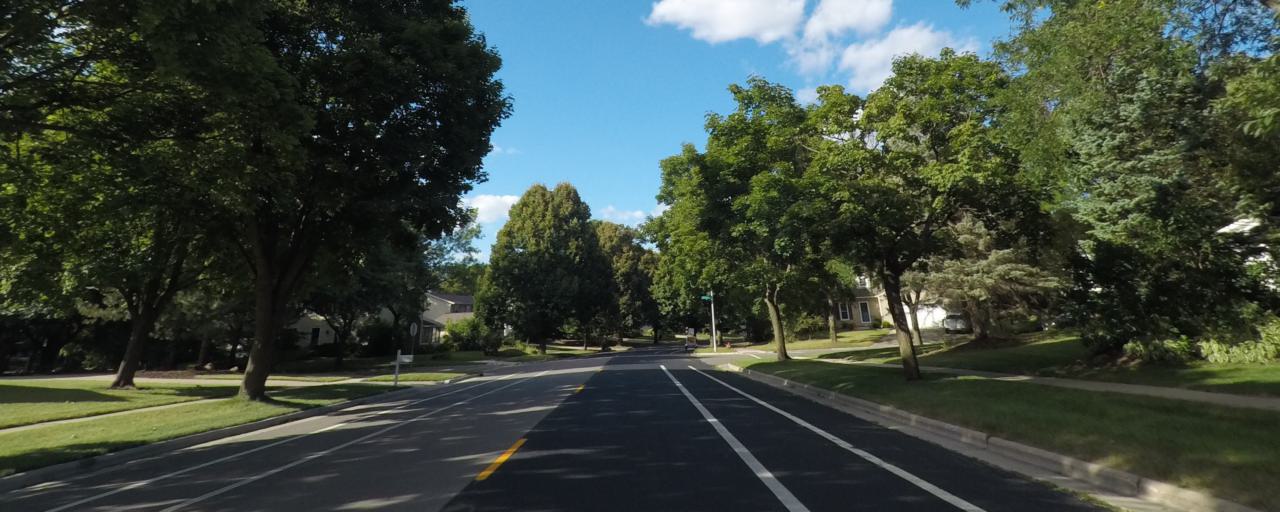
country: US
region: Wisconsin
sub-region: Dane County
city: Middleton
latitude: 43.0719
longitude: -89.5104
